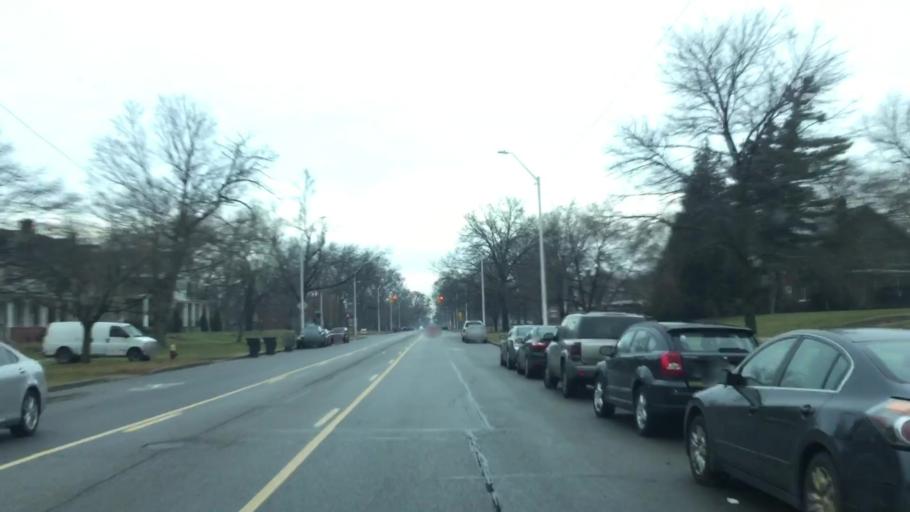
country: US
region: Michigan
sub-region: Wayne County
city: Detroit
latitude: 42.3564
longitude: -83.0079
